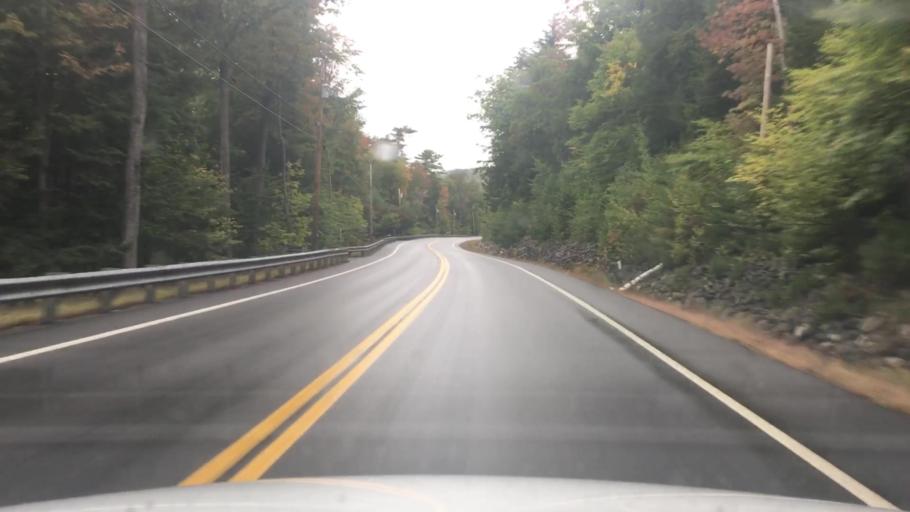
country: US
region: Maine
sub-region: Kennebec County
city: Rome
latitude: 44.5455
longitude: -69.8933
